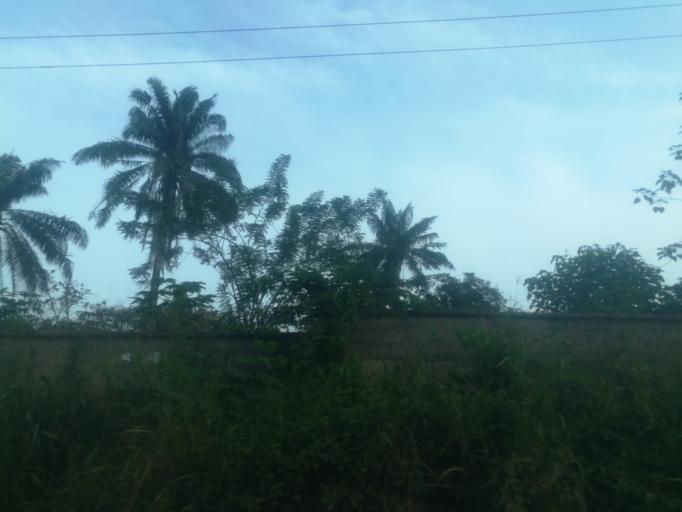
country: NG
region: Ogun
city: Abeokuta
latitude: 7.1288
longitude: 3.3266
